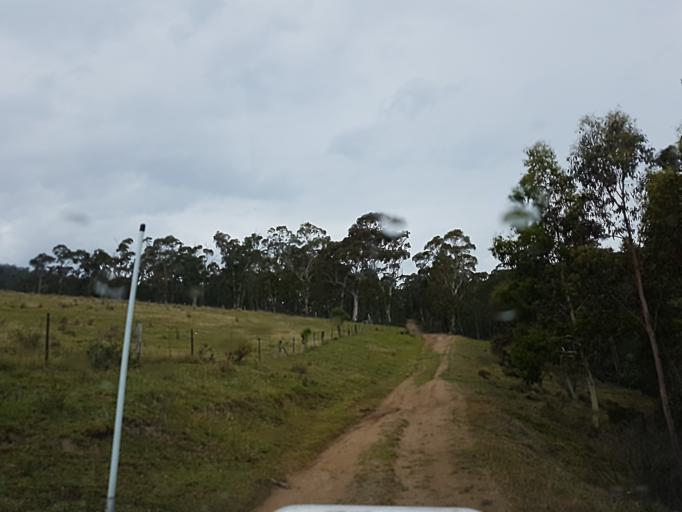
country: AU
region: New South Wales
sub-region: Snowy River
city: Jindabyne
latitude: -36.8659
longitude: 148.3269
